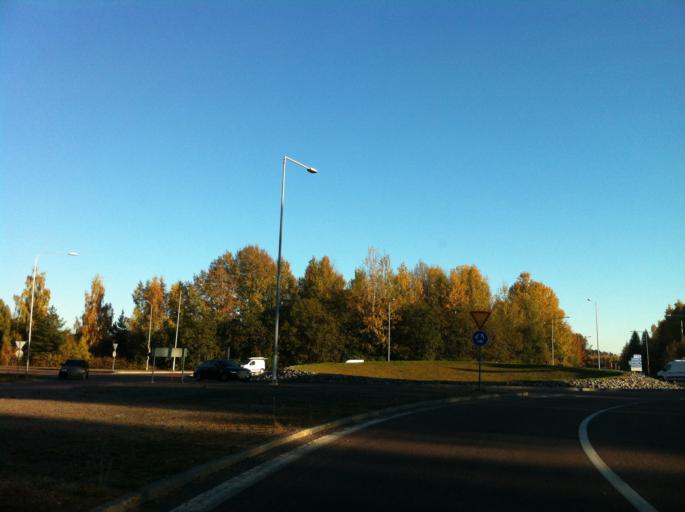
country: SE
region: Dalarna
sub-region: Faluns Kommun
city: Falun
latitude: 60.6263
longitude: 15.6105
